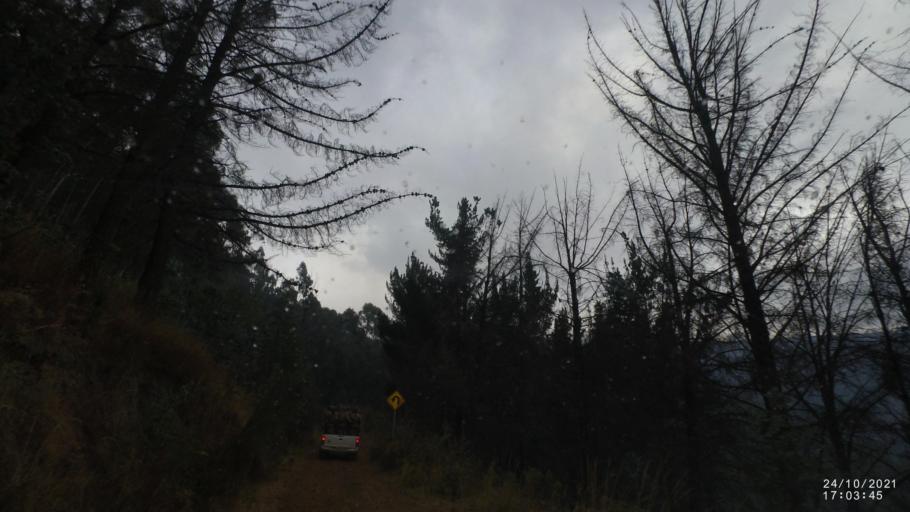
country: BO
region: Cochabamba
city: Cochabamba
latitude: -17.3363
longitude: -66.1393
